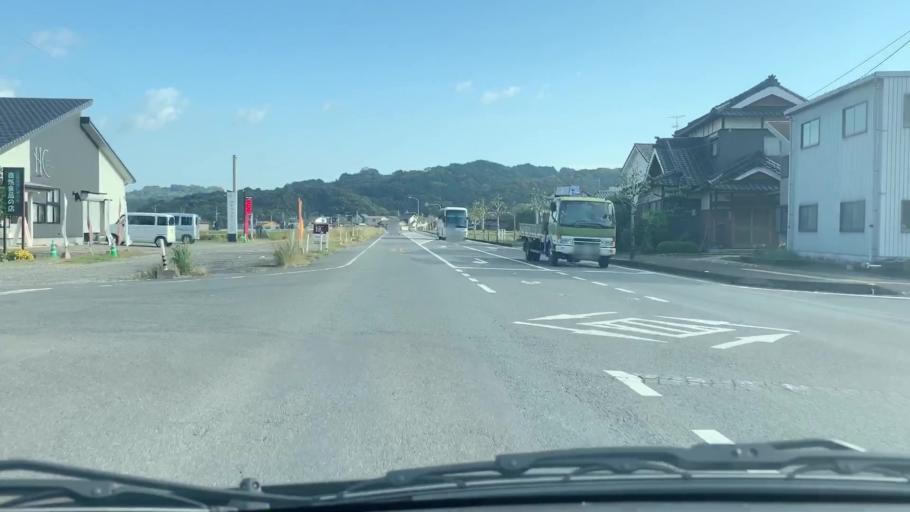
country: JP
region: Saga Prefecture
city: Kashima
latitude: 33.0935
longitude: 130.0946
